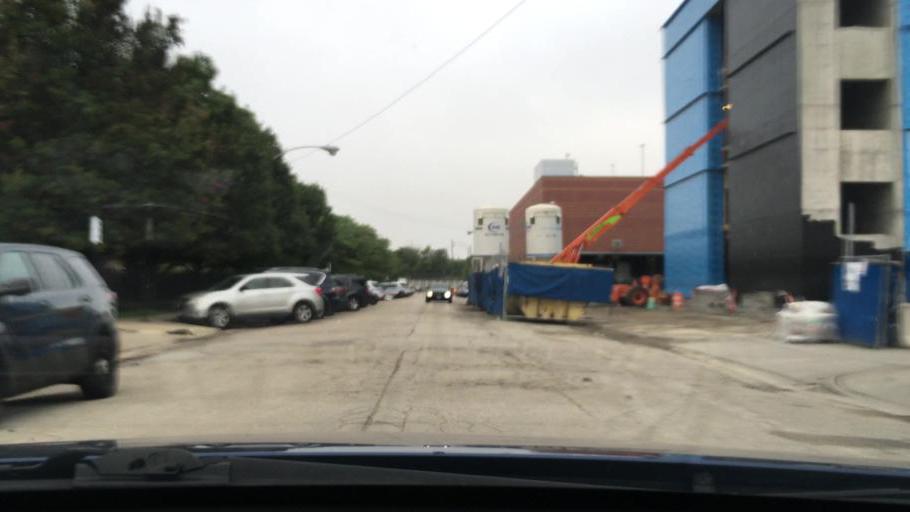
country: US
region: Illinois
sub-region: Cook County
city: Chicago
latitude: 41.8590
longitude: -87.6265
